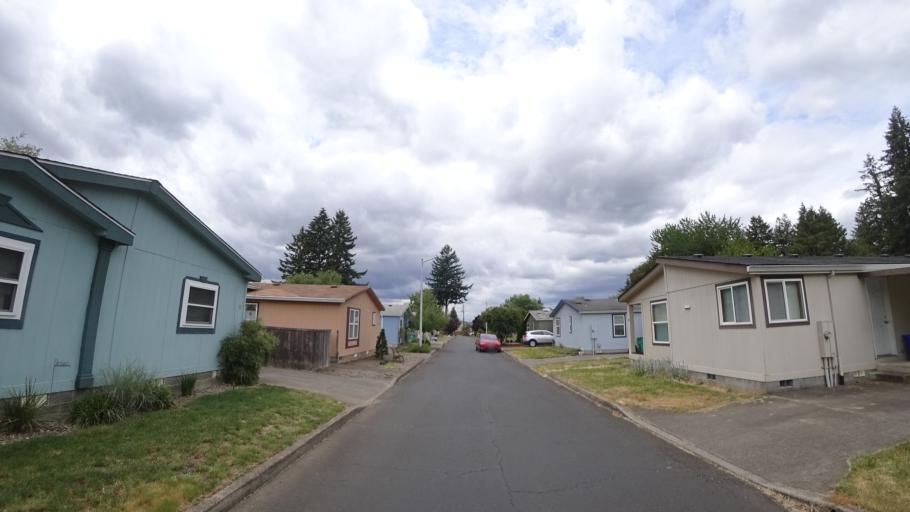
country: US
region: Oregon
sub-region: Clackamas County
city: Happy Valley
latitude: 45.4850
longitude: -122.5265
